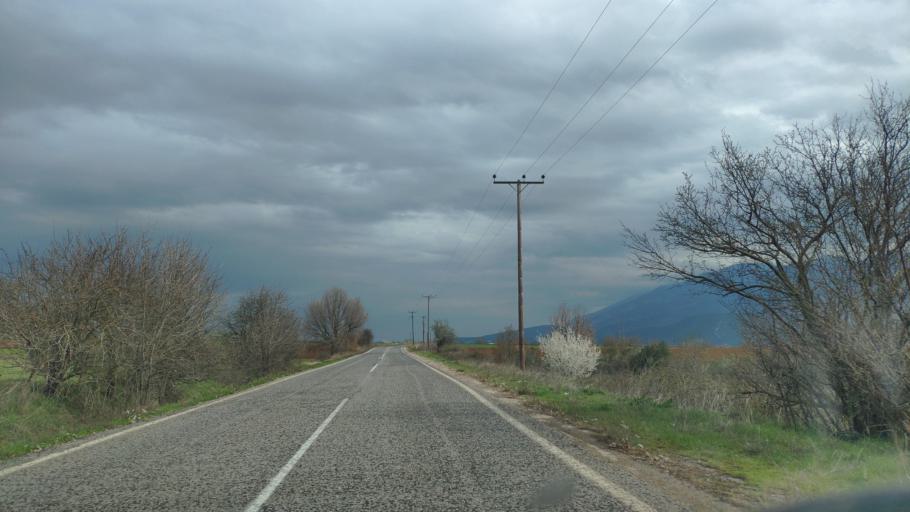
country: GR
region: Central Greece
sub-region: Nomos Fthiotidos
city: Amfikleia
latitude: 38.6997
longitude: 22.5160
